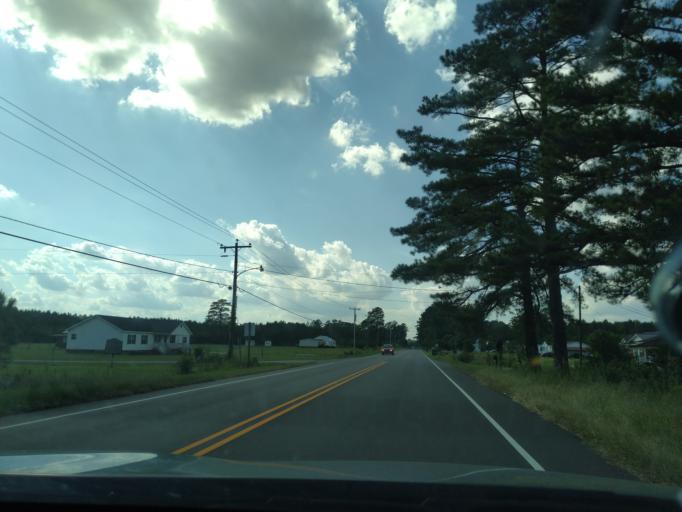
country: US
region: North Carolina
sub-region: Martin County
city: Robersonville
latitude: 35.8237
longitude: -77.3146
